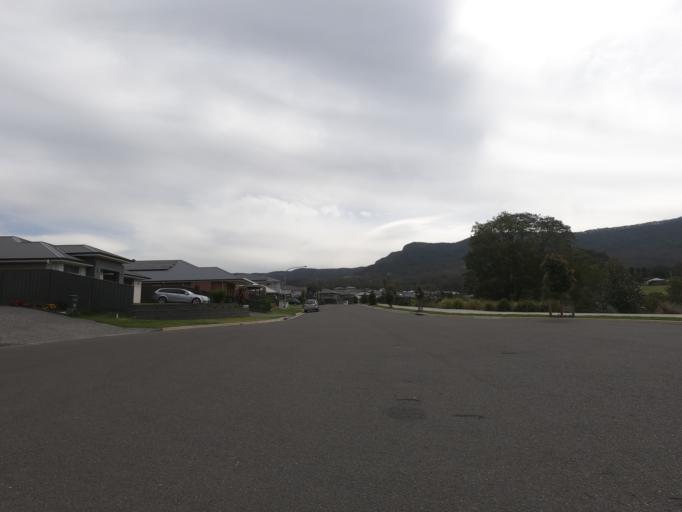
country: AU
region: New South Wales
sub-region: Wollongong
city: Dapto
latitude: -34.4941
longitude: 150.7582
